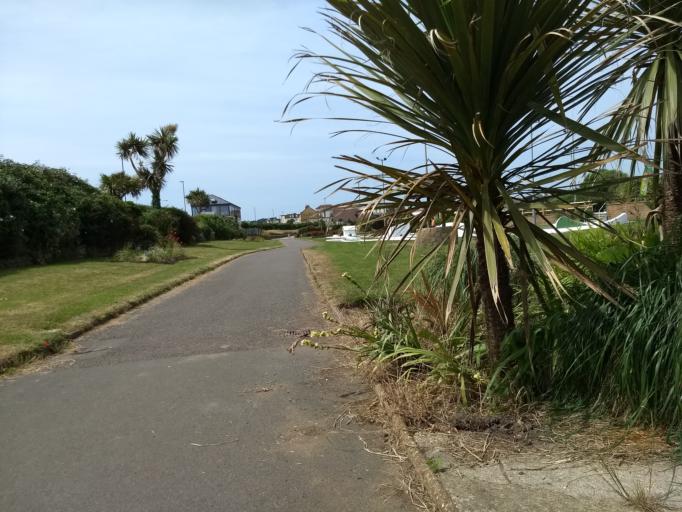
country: GB
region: England
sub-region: Isle of Wight
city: Sandown
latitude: 50.6581
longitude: -1.1448
